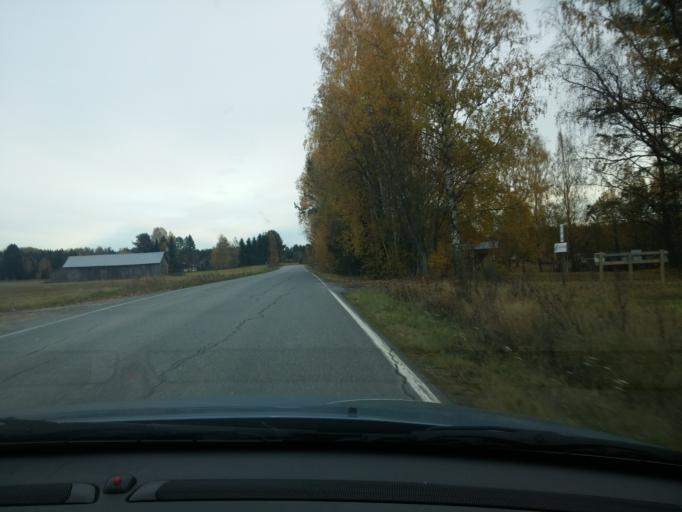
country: FI
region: Haeme
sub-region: Forssa
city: Tammela
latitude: 60.7666
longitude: 23.8534
